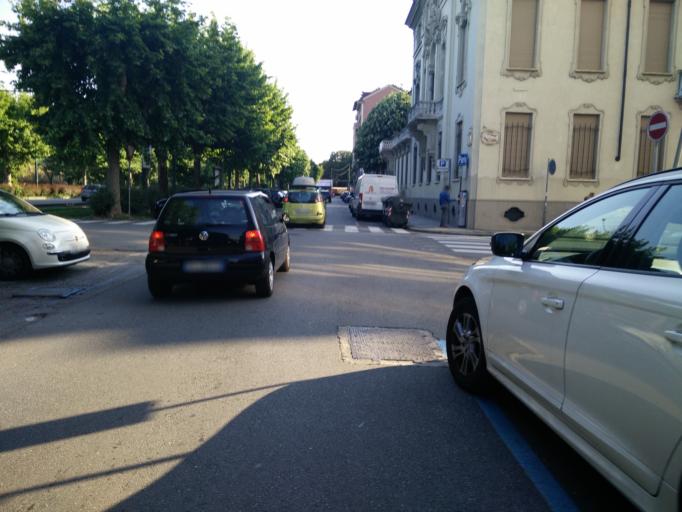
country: IT
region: Piedmont
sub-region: Provincia di Torino
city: Turin
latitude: 45.0604
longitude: 7.6919
